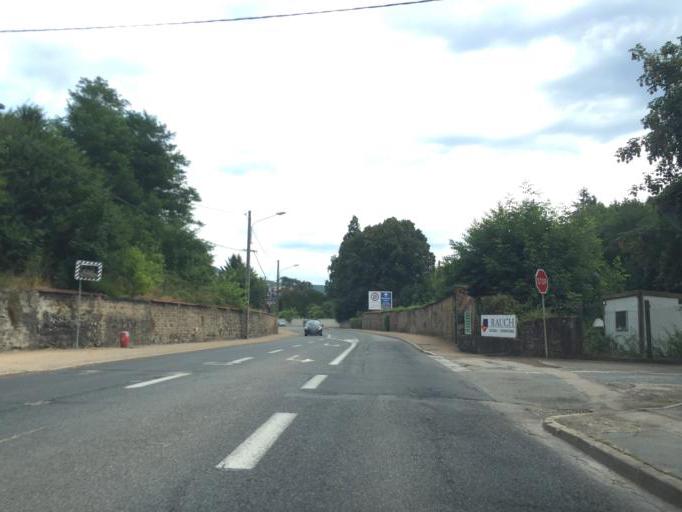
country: FR
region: Rhone-Alpes
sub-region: Departement du Rhone
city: Tarare
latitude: 45.8929
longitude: 4.4153
